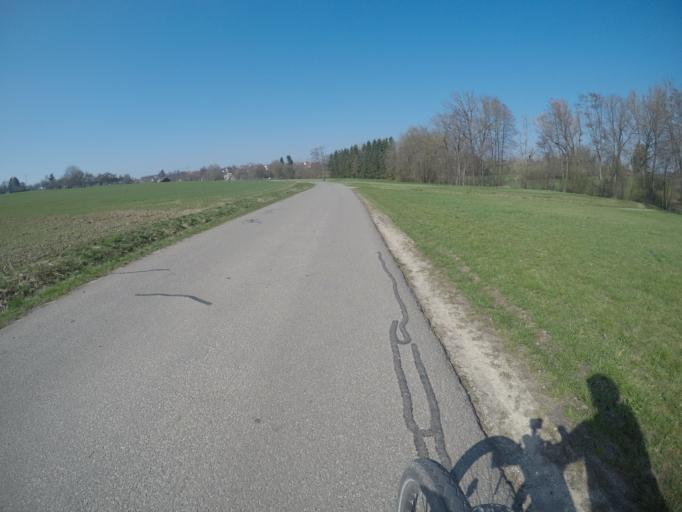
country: DE
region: Baden-Wuerttemberg
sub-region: Tuebingen Region
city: Pliezhausen
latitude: 48.5766
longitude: 9.2046
